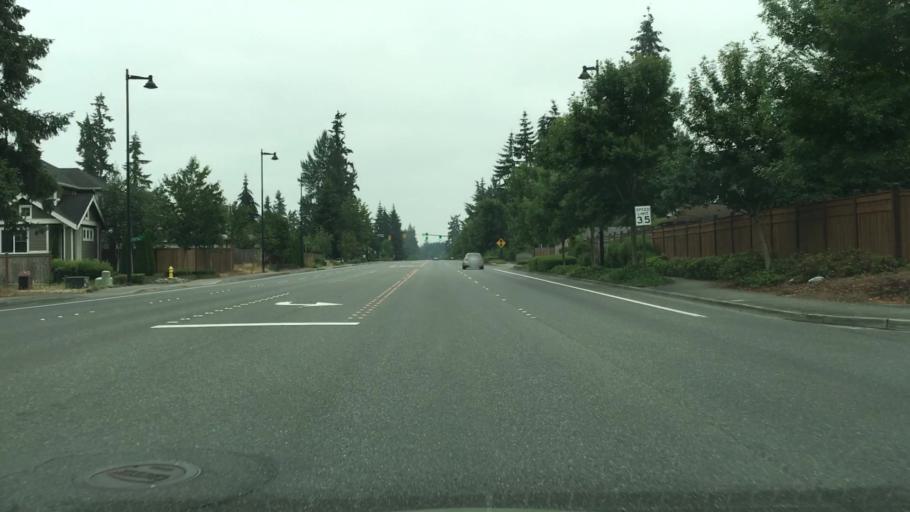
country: US
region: Washington
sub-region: King County
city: Newcastle
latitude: 47.5129
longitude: -122.1558
